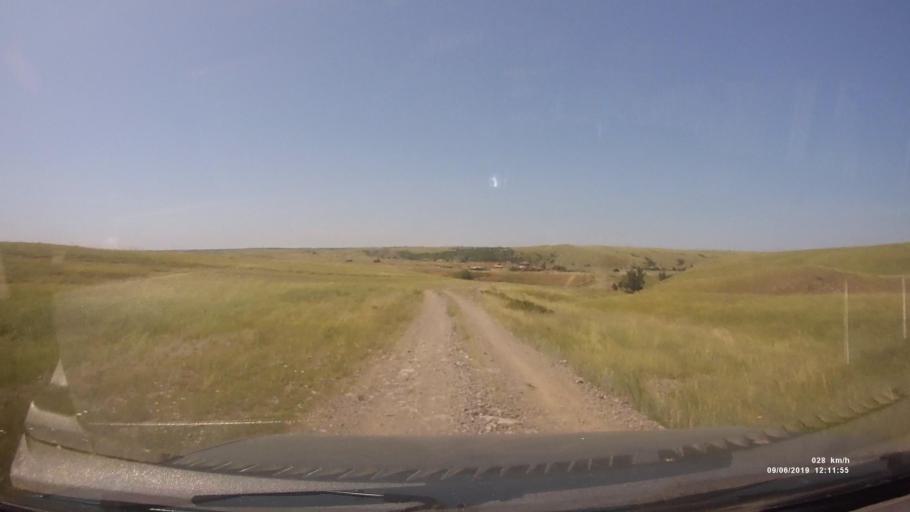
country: RU
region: Rostov
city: Staraya Stanitsa
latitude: 48.2504
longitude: 40.3293
